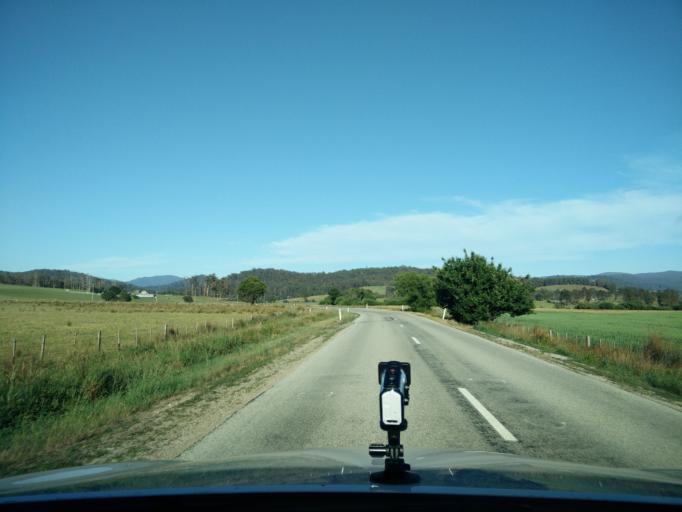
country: AU
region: Tasmania
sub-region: Break O'Day
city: St Helens
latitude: -41.2720
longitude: 148.1070
